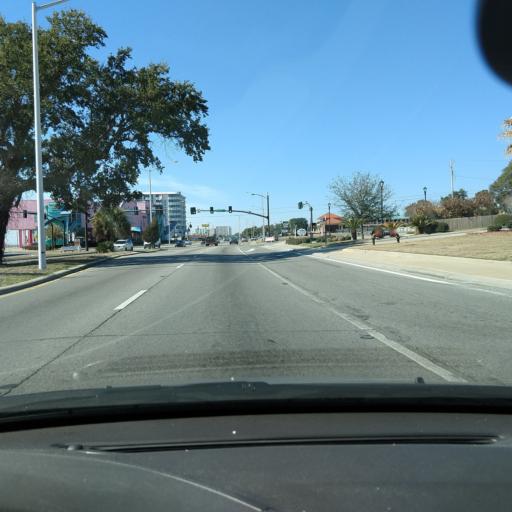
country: US
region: Mississippi
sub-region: Harrison County
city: Biloxi
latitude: 30.3937
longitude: -88.9376
